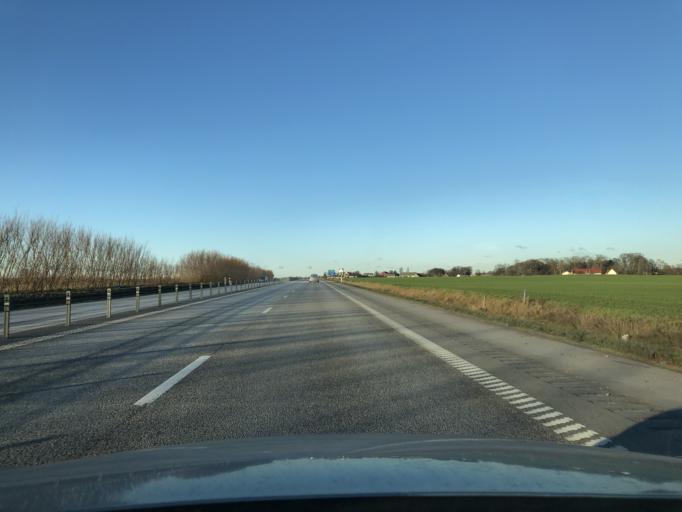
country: SE
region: Skane
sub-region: Trelleborgs Kommun
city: Skare
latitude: 55.3954
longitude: 13.0715
